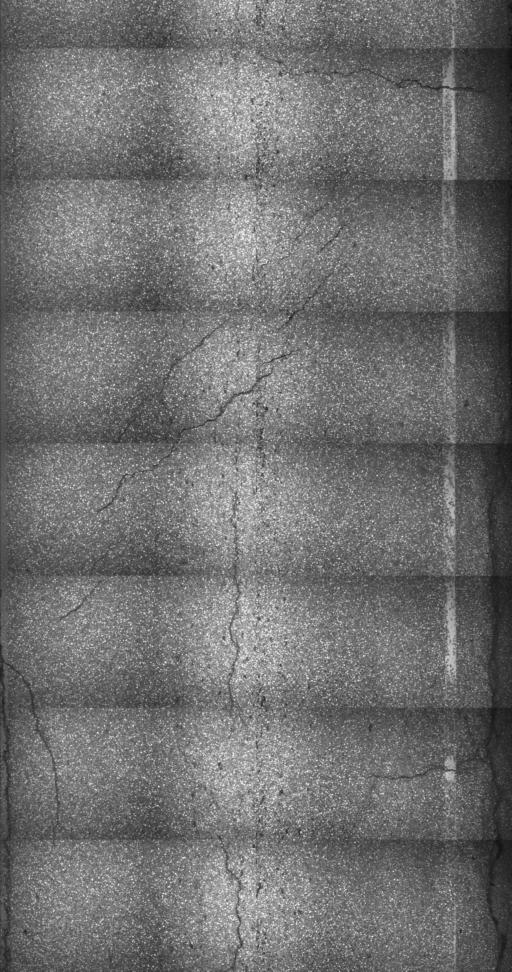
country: US
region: Vermont
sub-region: Franklin County
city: Saint Albans
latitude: 44.8021
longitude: -73.0609
